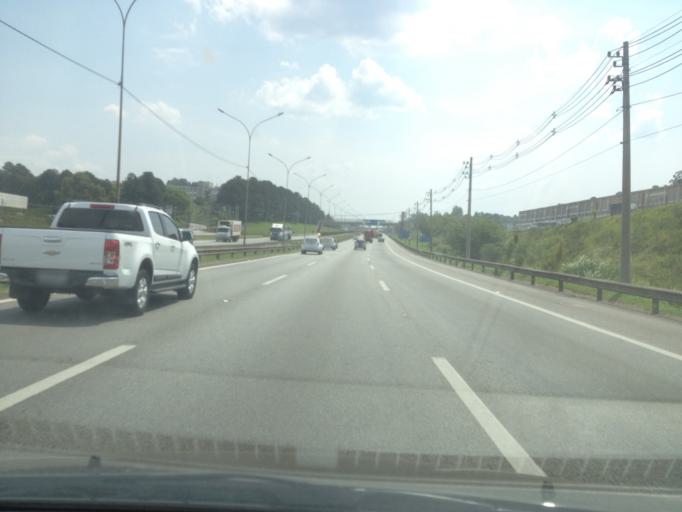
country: BR
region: Sao Paulo
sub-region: Jandira
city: Jandira
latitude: -23.5171
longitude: -46.9312
